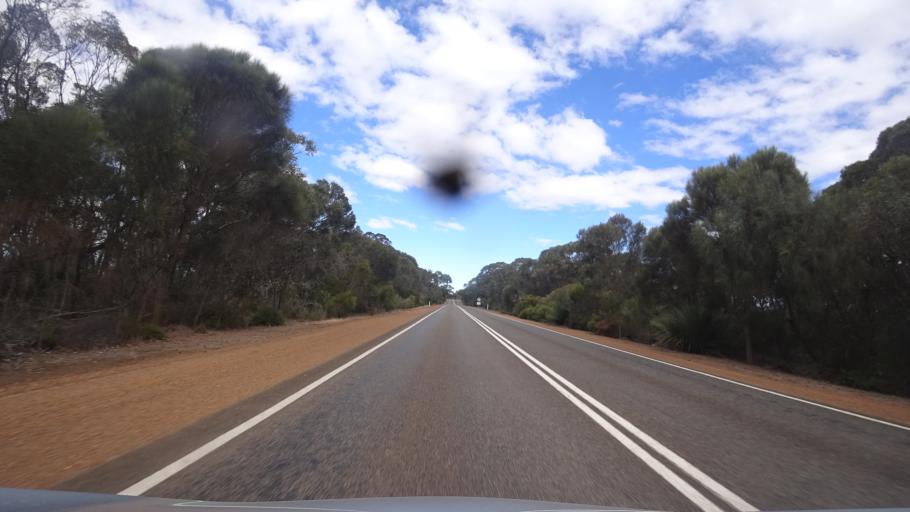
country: AU
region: South Australia
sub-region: Kangaroo Island
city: Kingscote
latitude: -35.7604
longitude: 137.3669
